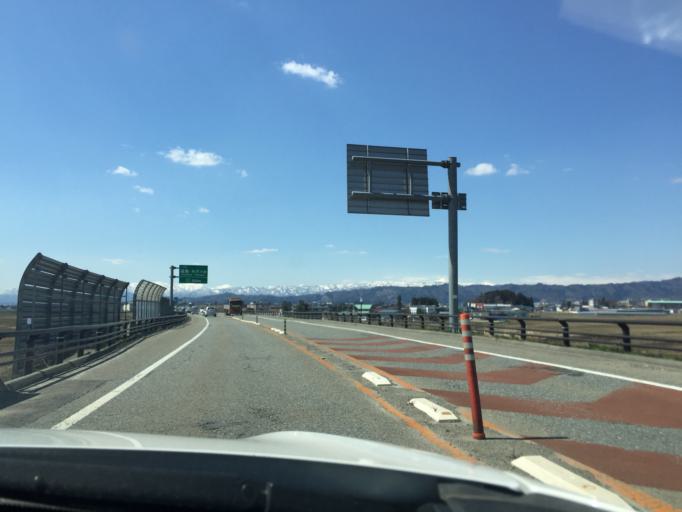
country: JP
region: Yamagata
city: Takahata
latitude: 38.0284
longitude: 140.1657
